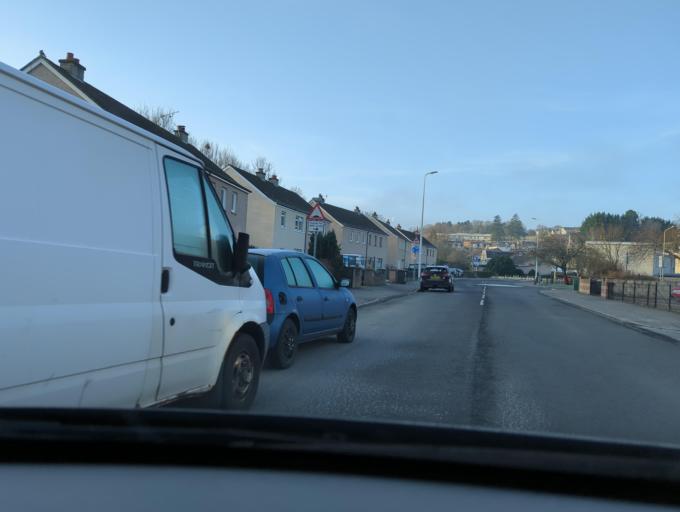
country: GB
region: Scotland
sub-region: Perth and Kinross
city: Perth
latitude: 56.4014
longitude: -3.4545
